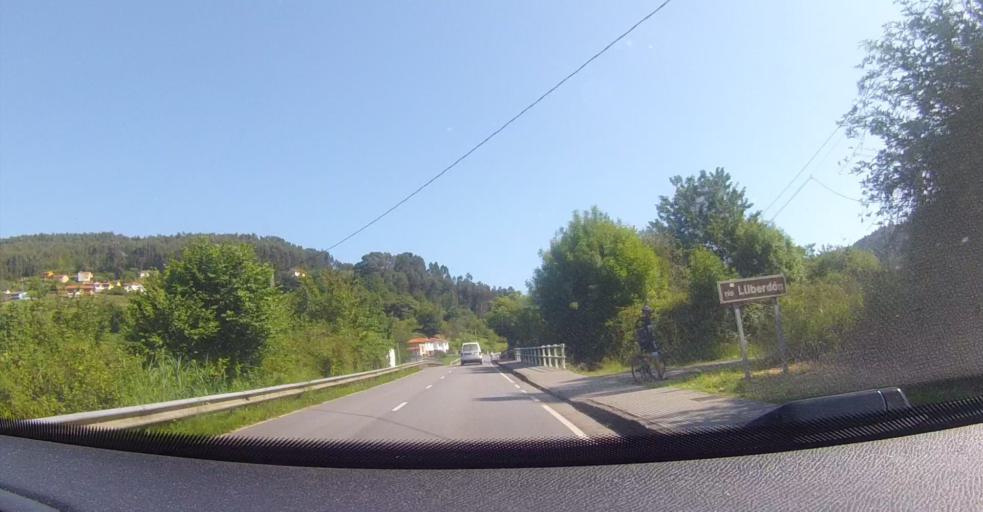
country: ES
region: Asturias
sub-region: Province of Asturias
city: Colunga
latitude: 43.4912
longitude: -5.2683
